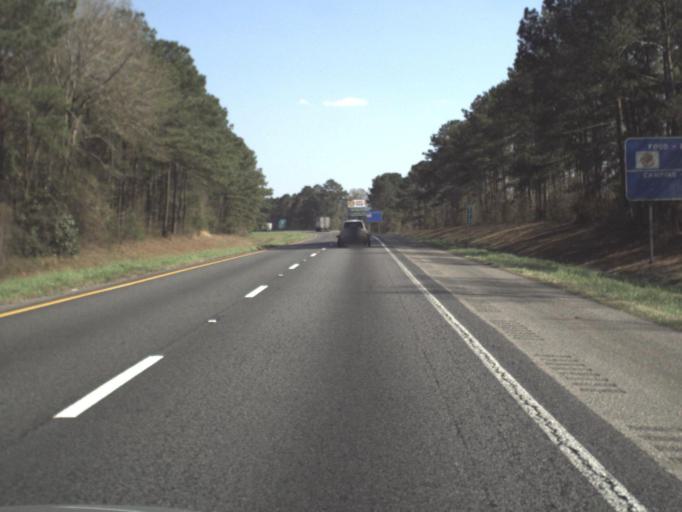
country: US
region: Florida
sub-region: Gadsden County
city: Gretna
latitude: 30.5829
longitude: -84.7115
